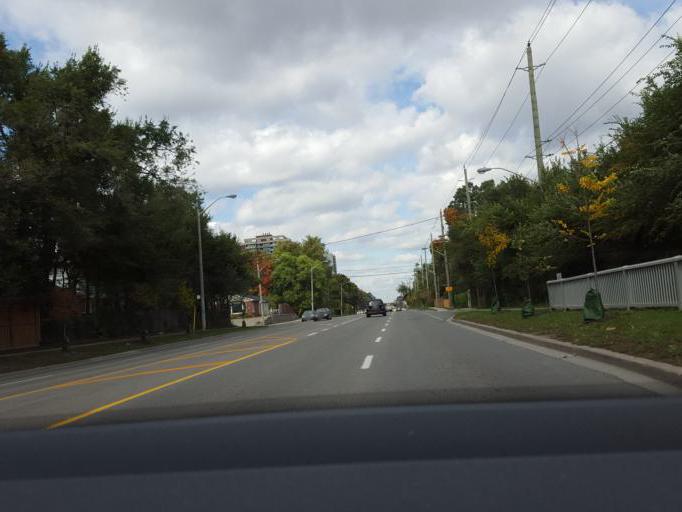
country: CA
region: Ontario
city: Willowdale
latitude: 43.7491
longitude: -79.3592
